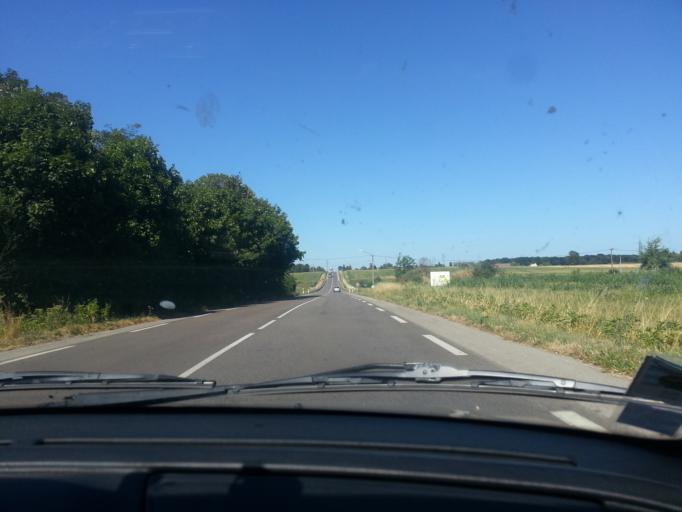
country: FR
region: Bourgogne
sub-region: Departement de Saone-et-Loire
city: Sassenay
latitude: 46.8026
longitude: 4.9391
